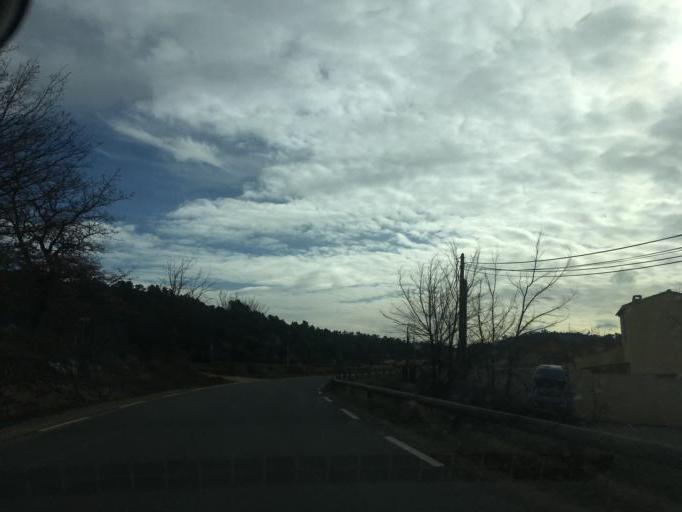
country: FR
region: Provence-Alpes-Cote d'Azur
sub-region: Departement du Var
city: Bras
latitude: 43.4686
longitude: 5.9603
